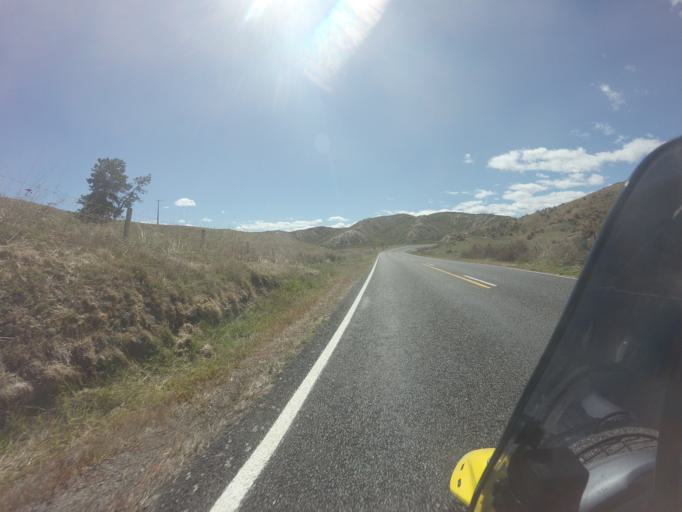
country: NZ
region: Bay of Plenty
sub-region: Whakatane District
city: Murupara
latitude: -38.3169
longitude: 176.7993
